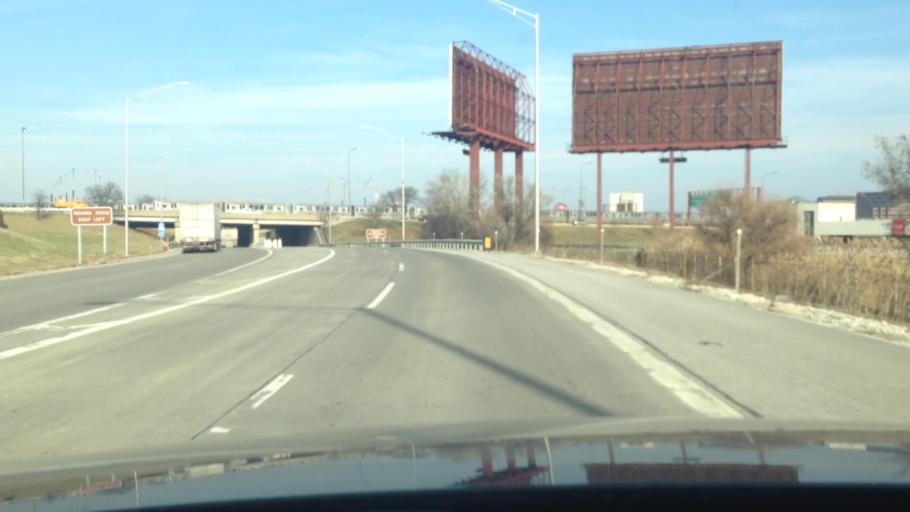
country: US
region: Illinois
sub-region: Cook County
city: Rosemont
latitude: 41.9815
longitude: -87.8680
